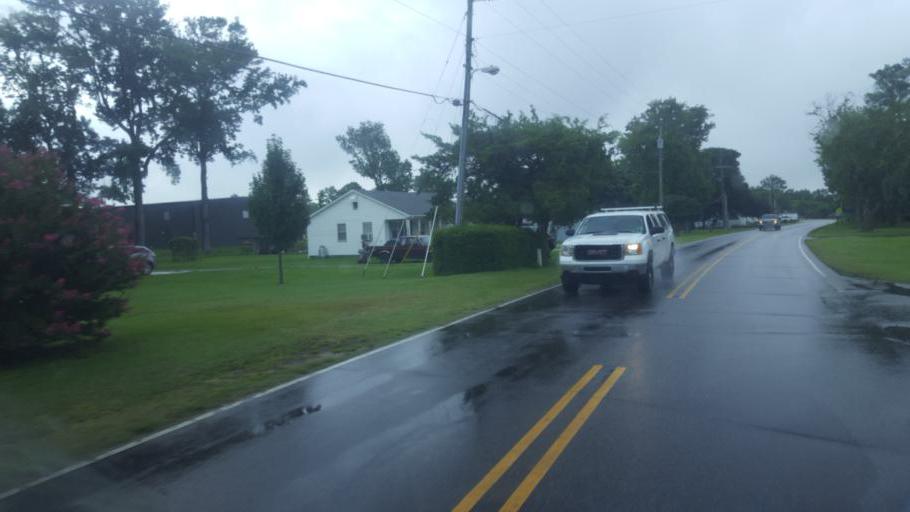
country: US
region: North Carolina
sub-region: Dare County
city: Wanchese
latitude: 35.8435
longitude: -75.6326
